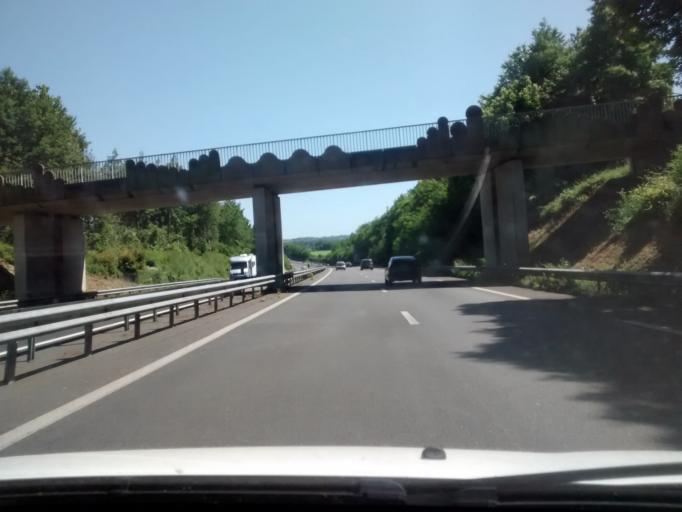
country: FR
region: Brittany
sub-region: Departement d'Ille-et-Vilaine
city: Tinteniac
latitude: 48.3361
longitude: -1.8604
